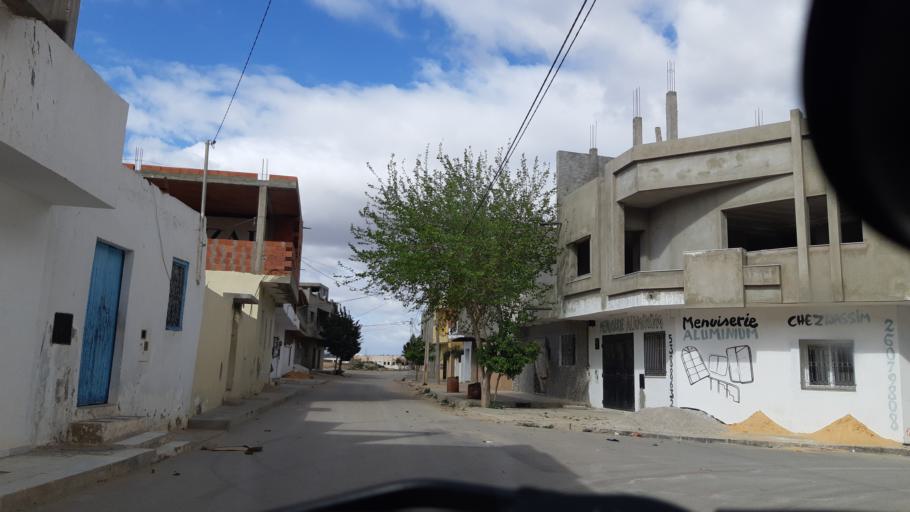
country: TN
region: Susah
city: Akouda
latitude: 35.8681
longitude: 10.5196
